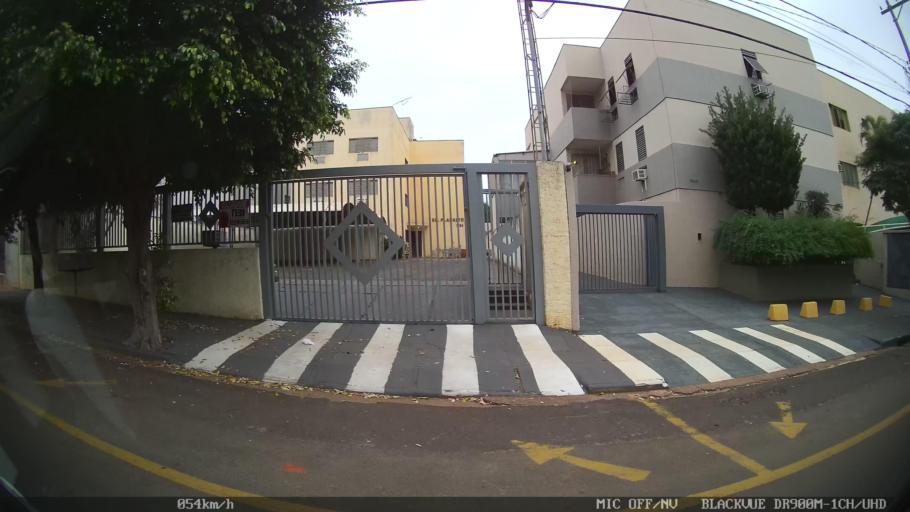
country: BR
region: Sao Paulo
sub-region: Sao Jose Do Rio Preto
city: Sao Jose do Rio Preto
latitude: -20.8423
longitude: -49.4023
